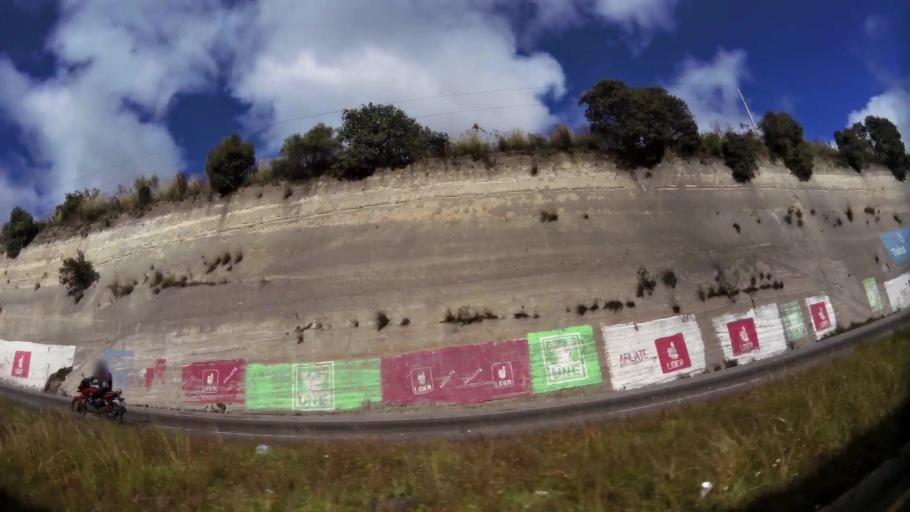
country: GT
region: Quetzaltenango
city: Salcaja
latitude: 14.8949
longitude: -91.4618
